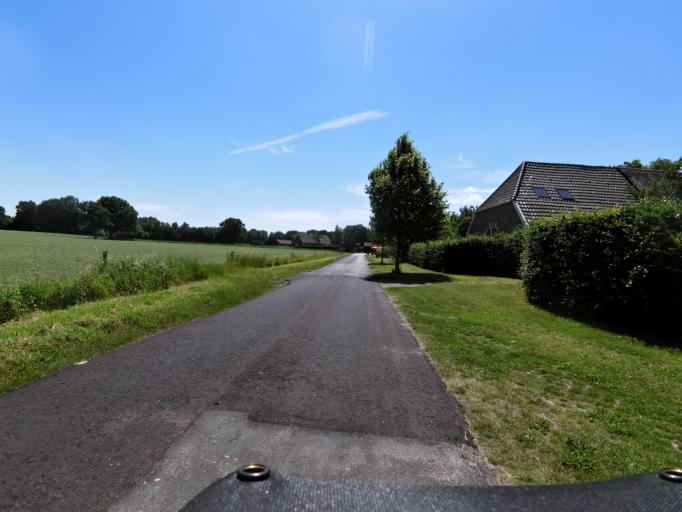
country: NL
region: Overijssel
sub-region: Gemeente Twenterand
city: Den Ham
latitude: 52.4961
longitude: 6.4035
